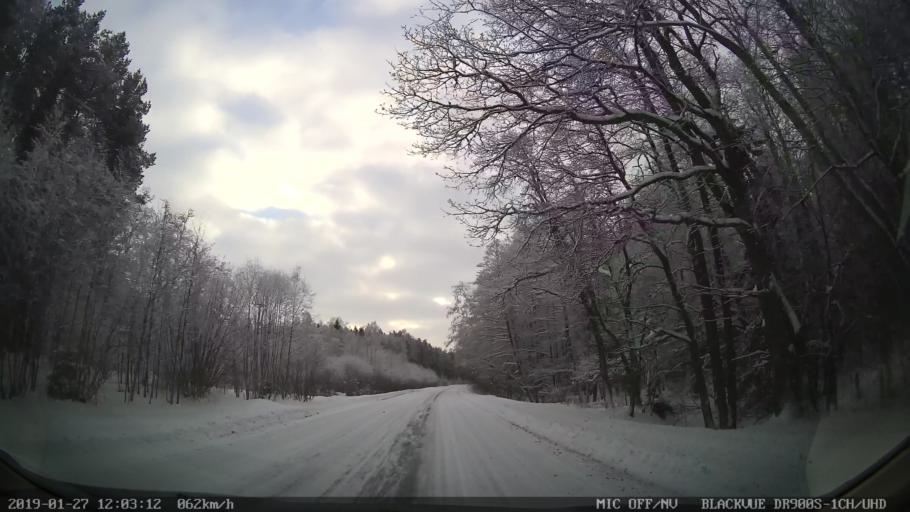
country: EE
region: Harju
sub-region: Raasiku vald
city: Raasiku
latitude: 59.4936
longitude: 25.2621
